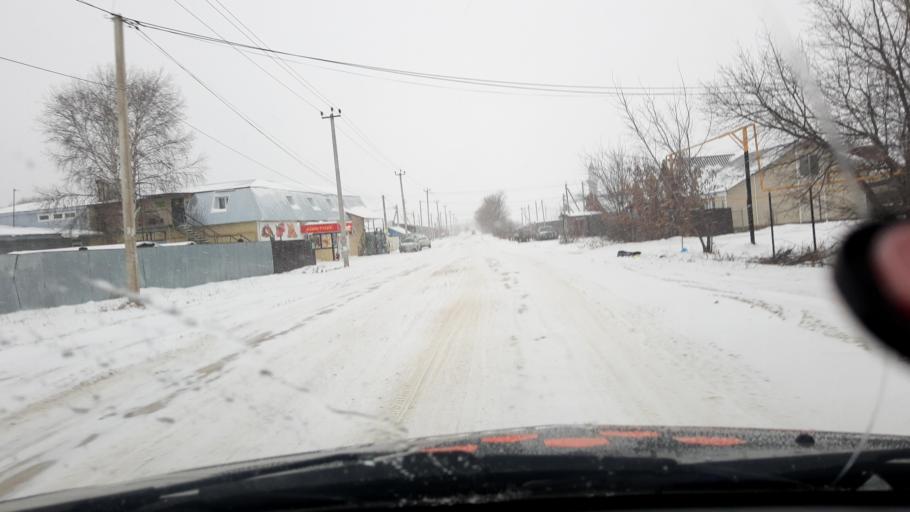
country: RU
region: Bashkortostan
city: Ufa
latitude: 54.5433
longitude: 55.9332
